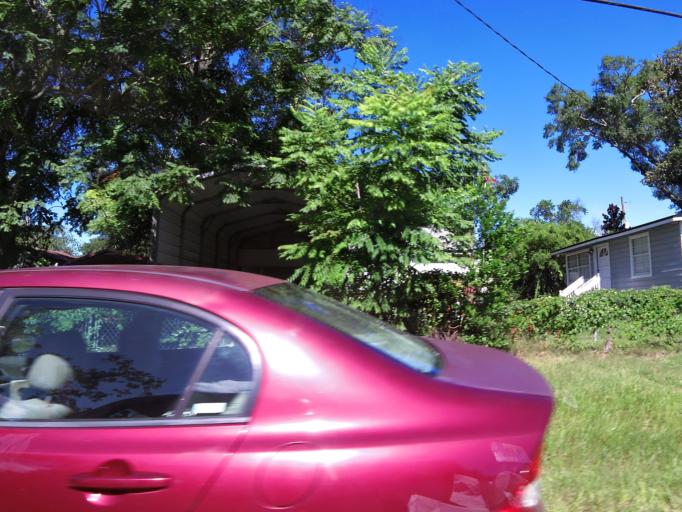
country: US
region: Florida
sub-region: Duval County
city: Jacksonville
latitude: 30.2750
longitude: -81.7261
